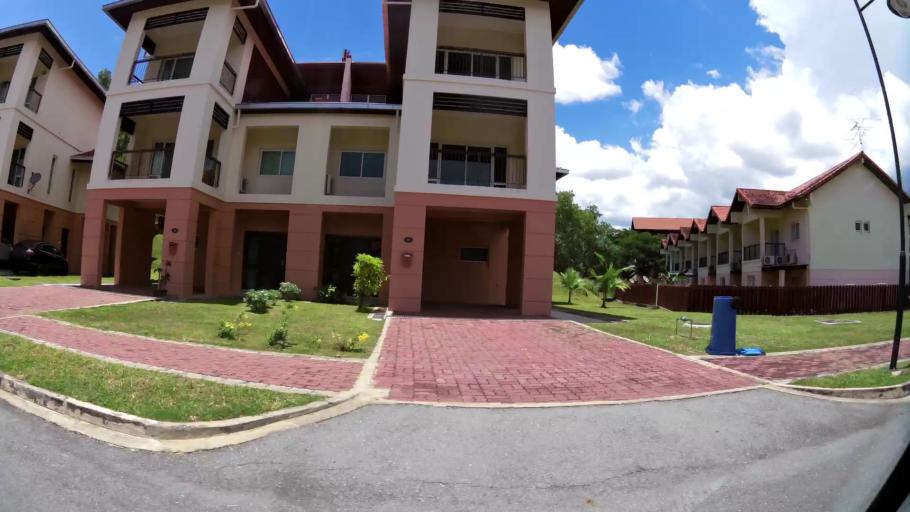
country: BN
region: Brunei and Muara
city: Bandar Seri Begawan
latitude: 4.9542
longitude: 114.8930
